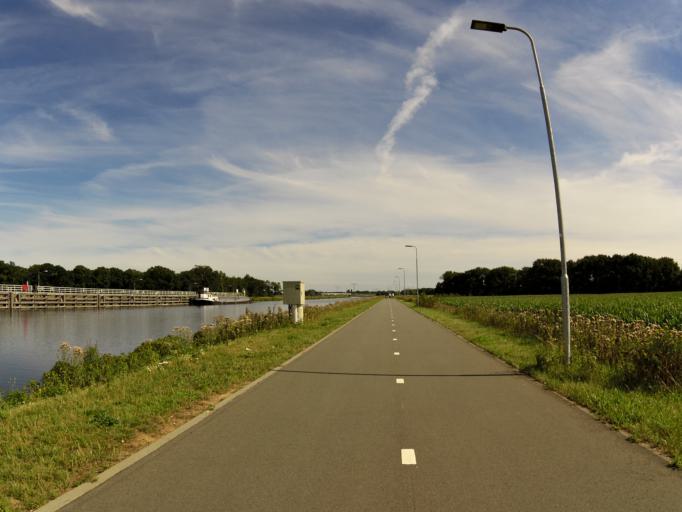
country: NL
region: North Brabant
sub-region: Gemeente 's-Hertogenbosch
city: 's-Hertogenbosch
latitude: 51.6973
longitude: 5.3591
